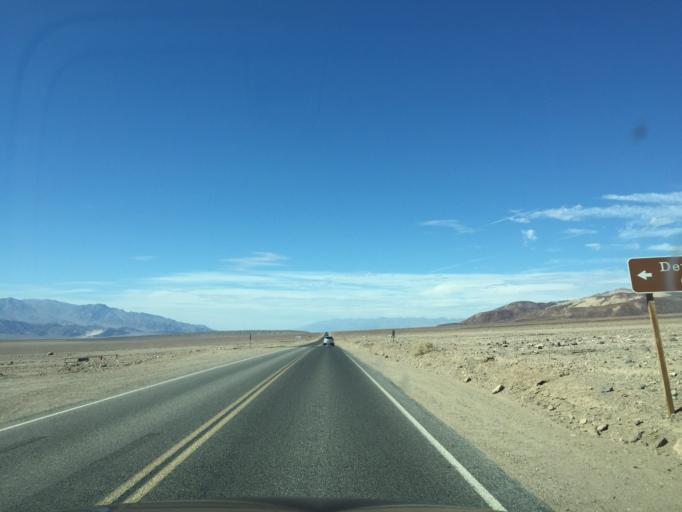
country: US
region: Nevada
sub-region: Nye County
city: Beatty
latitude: 36.2978
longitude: -116.8112
